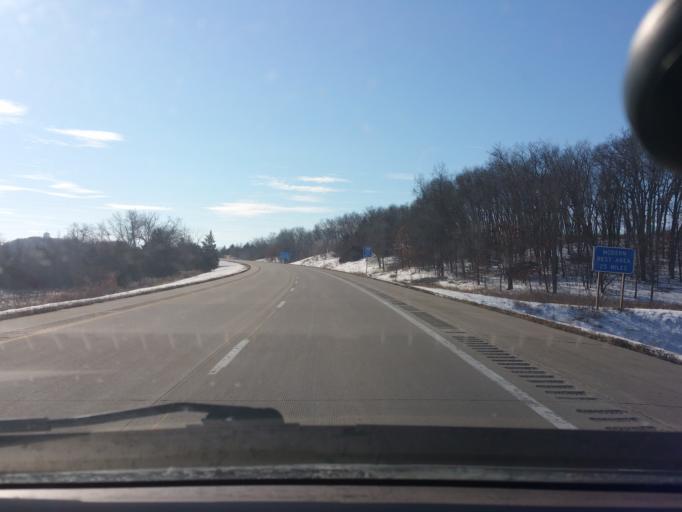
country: US
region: Iowa
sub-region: Clarke County
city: Osceola
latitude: 41.0027
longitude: -93.8000
